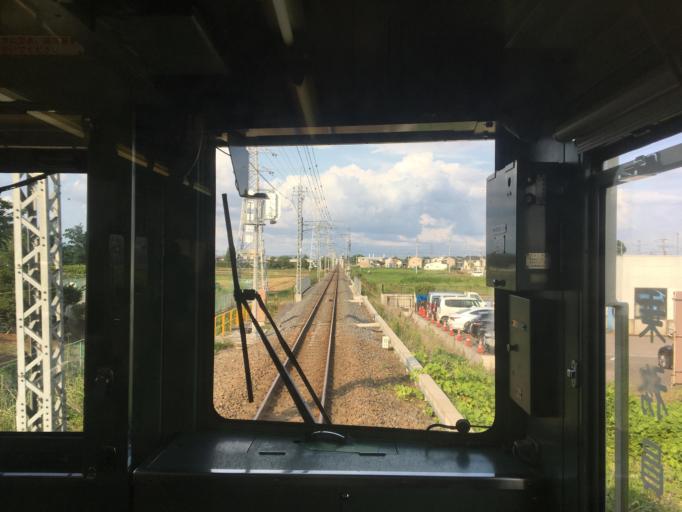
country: JP
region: Gunma
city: Ota
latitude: 36.2724
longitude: 139.3163
